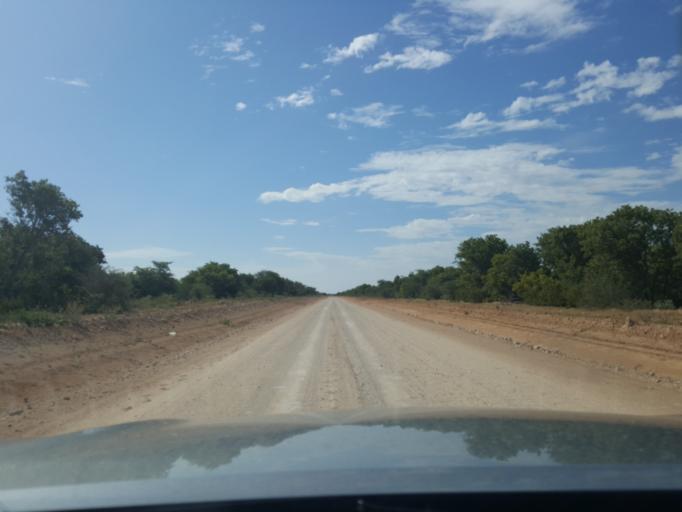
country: BW
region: Kweneng
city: Khudumelapye
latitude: -23.7567
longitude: 24.7581
